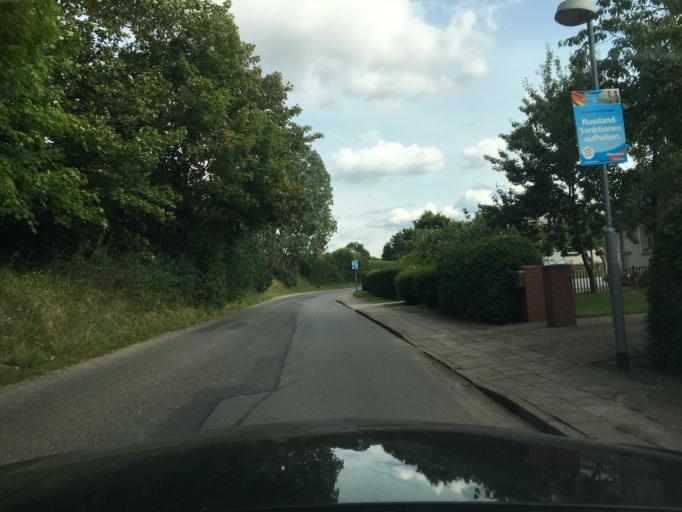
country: DE
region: Mecklenburg-Vorpommern
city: Mollenhagen
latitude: 53.4862
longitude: 12.9546
